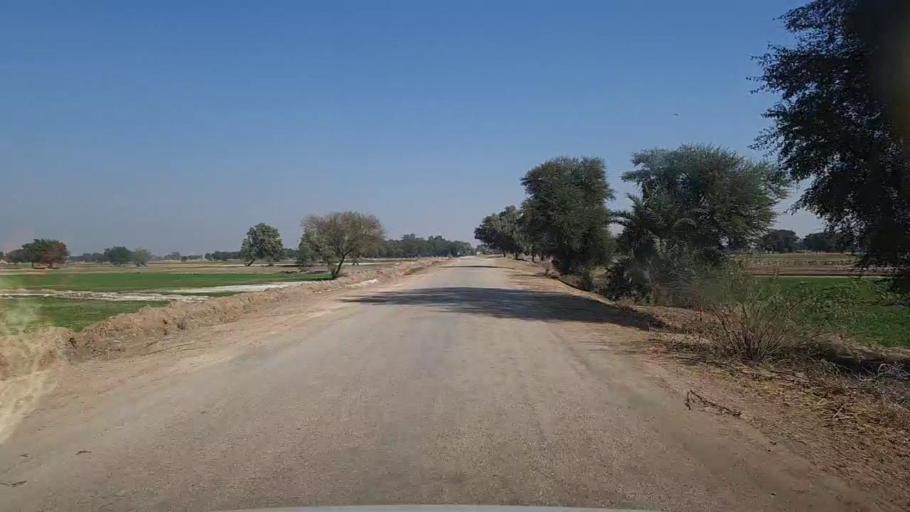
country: PK
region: Sindh
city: Khairpur
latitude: 27.9761
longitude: 69.8343
